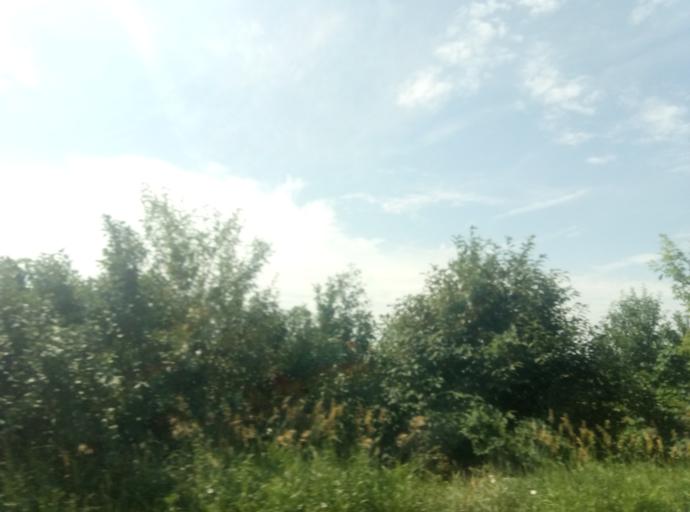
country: RU
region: Tula
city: Kireyevsk
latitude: 53.9226
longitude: 37.9491
